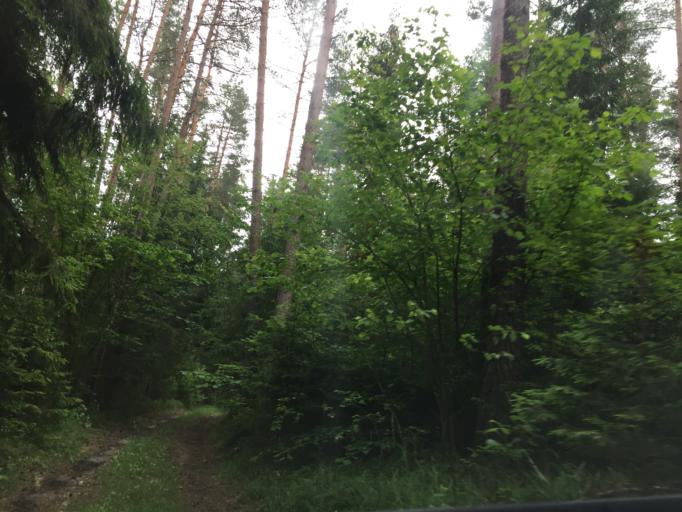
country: LV
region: Tukuma Rajons
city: Tukums
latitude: 57.0220
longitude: 23.0775
